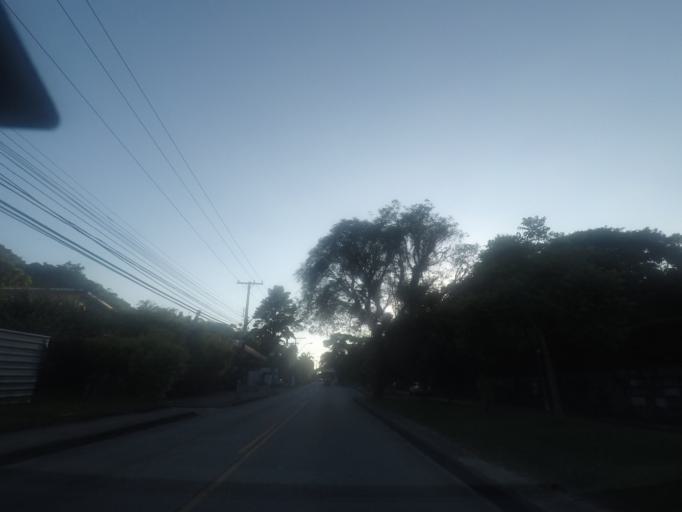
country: BR
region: Rio de Janeiro
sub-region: Petropolis
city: Petropolis
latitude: -22.5324
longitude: -43.2173
